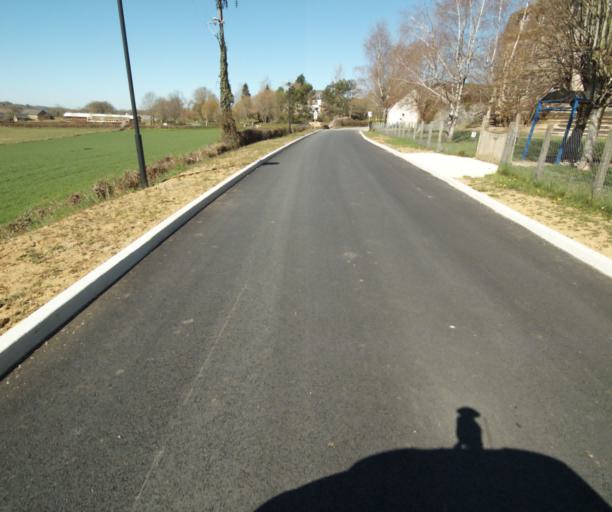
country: FR
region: Limousin
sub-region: Departement de la Correze
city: Chamboulive
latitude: 45.4310
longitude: 1.7026
